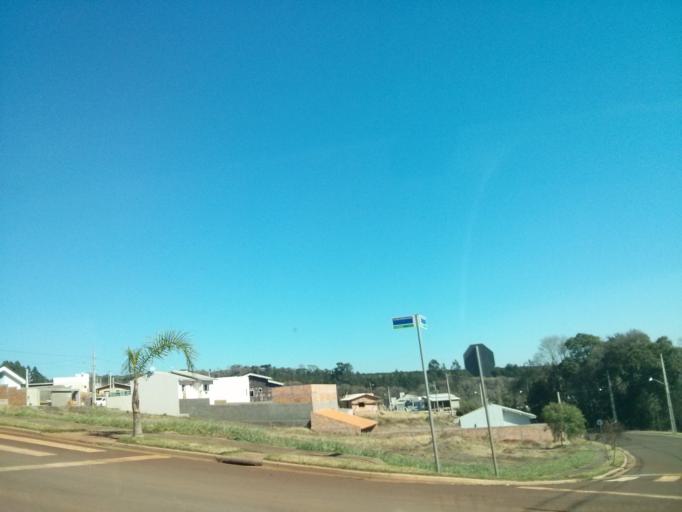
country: BR
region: Santa Catarina
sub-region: Chapeco
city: Chapeco
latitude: -27.0881
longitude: -52.7153
